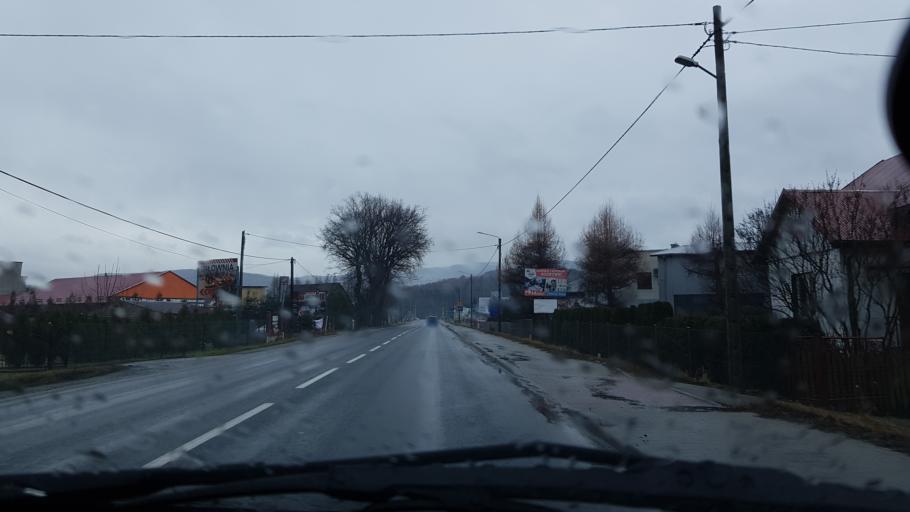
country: PL
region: Lesser Poland Voivodeship
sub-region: Powiat suski
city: Makow Podhalanski
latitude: 49.7150
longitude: 19.6881
